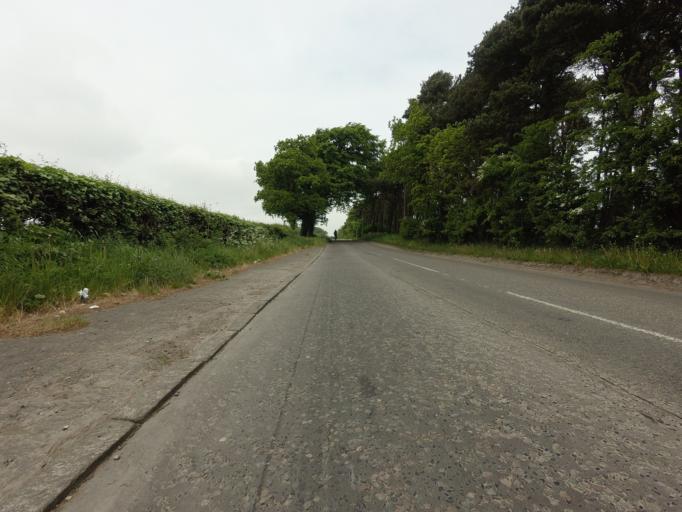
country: GB
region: Scotland
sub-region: Fife
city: Townhill
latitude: 56.0961
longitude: -3.4433
